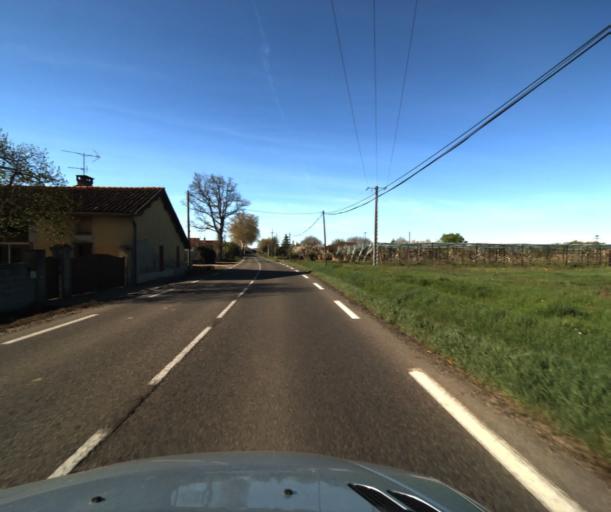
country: FR
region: Midi-Pyrenees
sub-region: Departement du Tarn-et-Garonne
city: Montbeton
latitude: 44.0622
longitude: 1.2885
